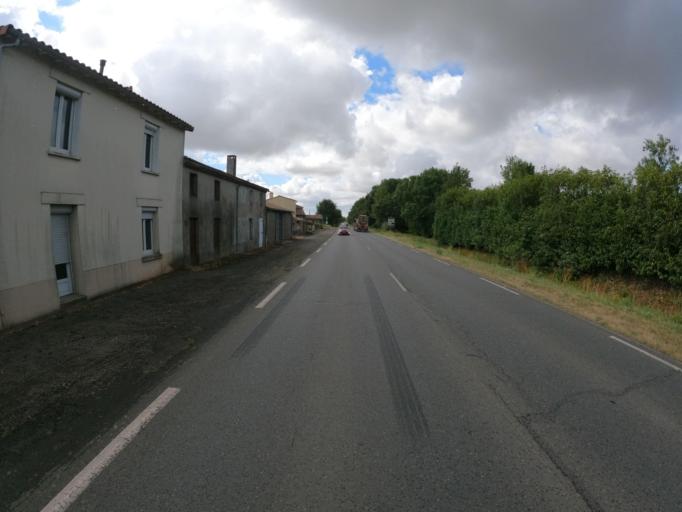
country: FR
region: Pays de la Loire
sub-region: Departement de la Loire-Atlantique
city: Mouzillon
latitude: 47.1204
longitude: -1.2827
